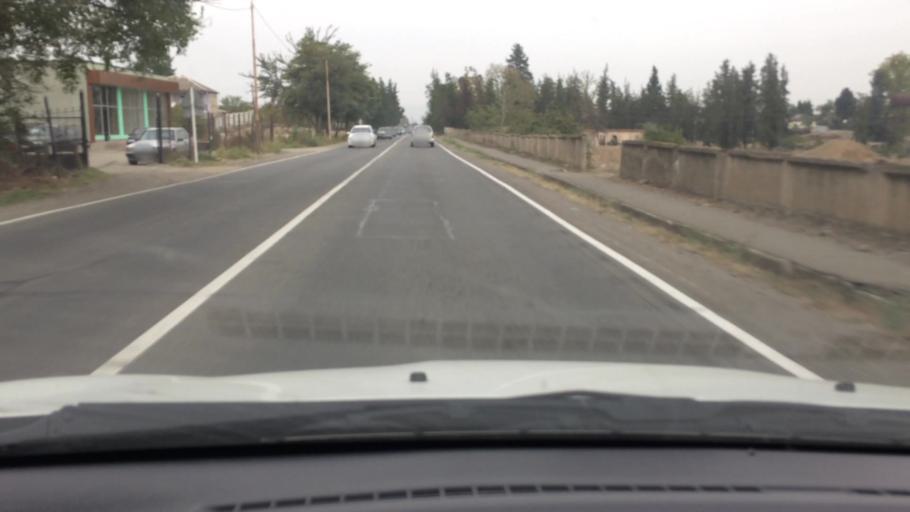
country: GE
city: Naghvarevi
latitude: 41.3685
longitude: 44.8379
